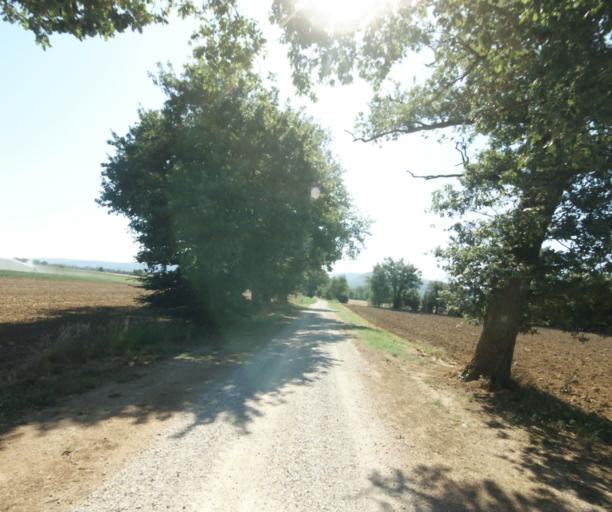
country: FR
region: Midi-Pyrenees
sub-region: Departement de la Haute-Garonne
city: Revel
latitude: 43.4610
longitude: 2.0352
